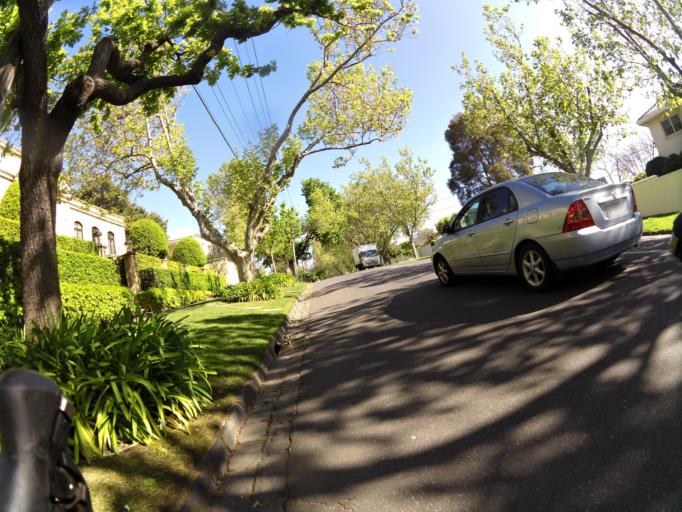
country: AU
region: Victoria
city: Toorak
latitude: -37.8367
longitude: 145.0194
